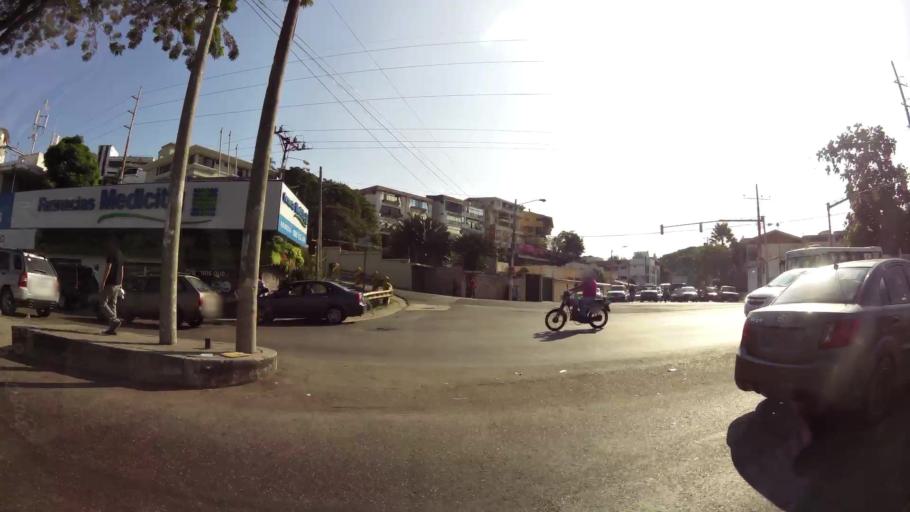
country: EC
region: Guayas
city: Guayaquil
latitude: -2.1675
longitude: -79.9031
